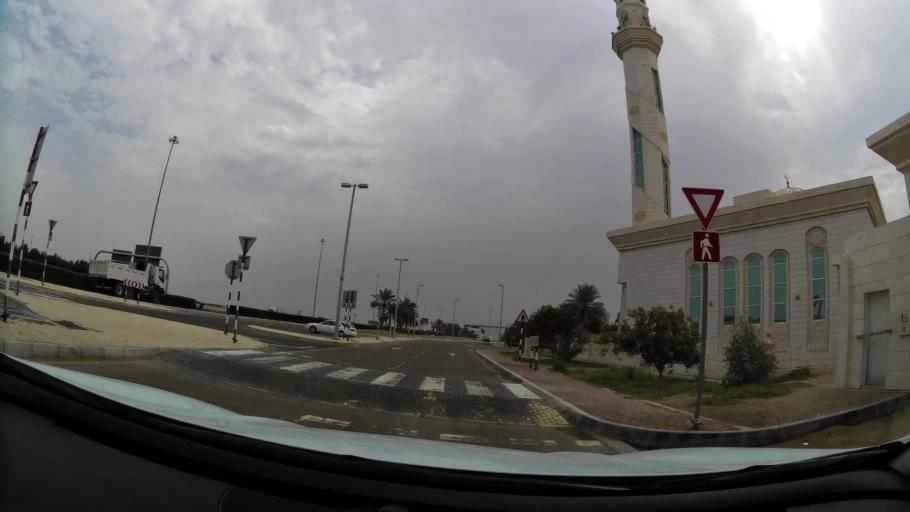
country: AE
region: Abu Dhabi
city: Abu Dhabi
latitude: 24.4411
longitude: 54.4496
